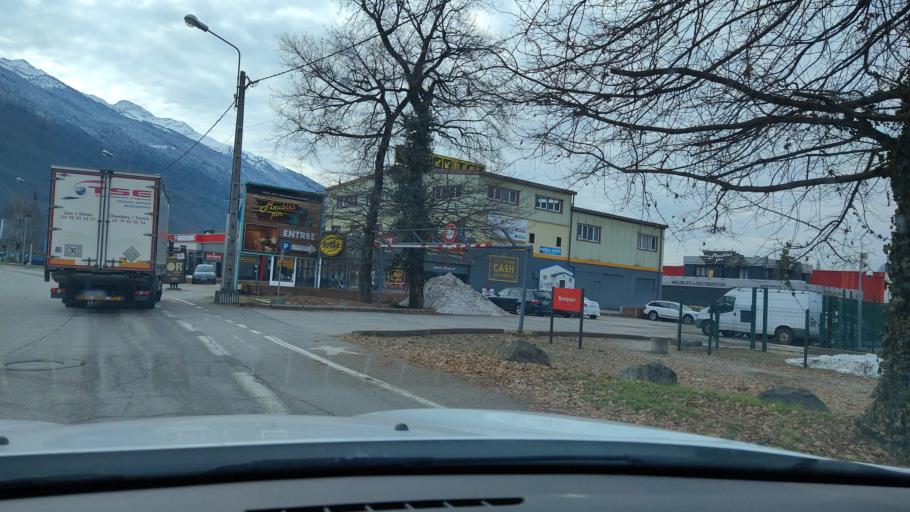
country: FR
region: Rhone-Alpes
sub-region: Departement de la Savoie
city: Grignon
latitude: 45.6576
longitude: 6.3694
